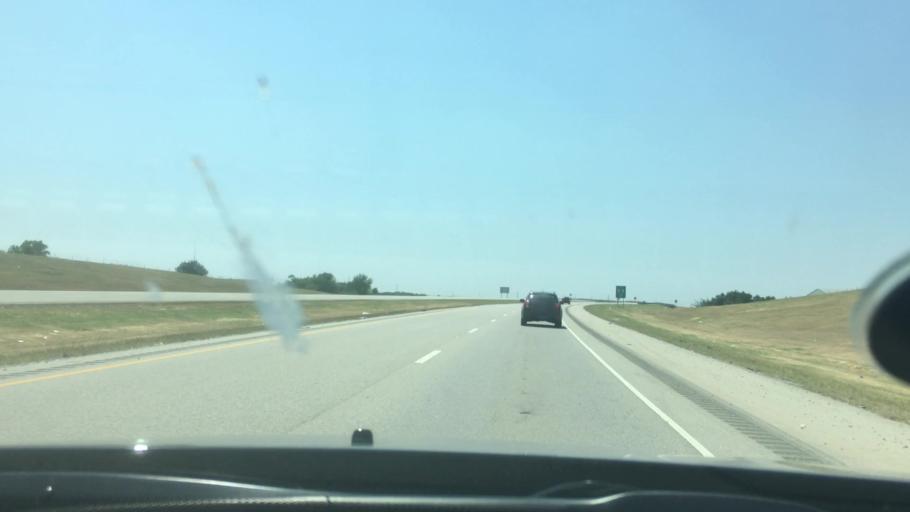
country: US
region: Oklahoma
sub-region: Bryan County
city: Calera
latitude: 33.9659
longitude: -96.4057
